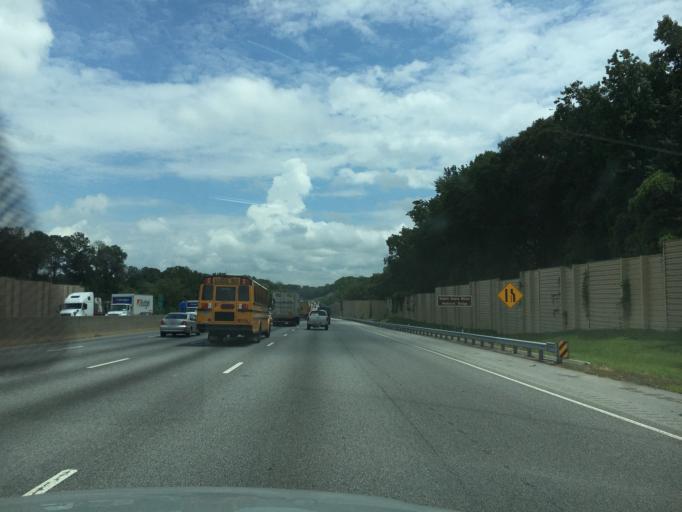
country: US
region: Georgia
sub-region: DeKalb County
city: Panthersville
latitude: 33.7076
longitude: -84.2041
